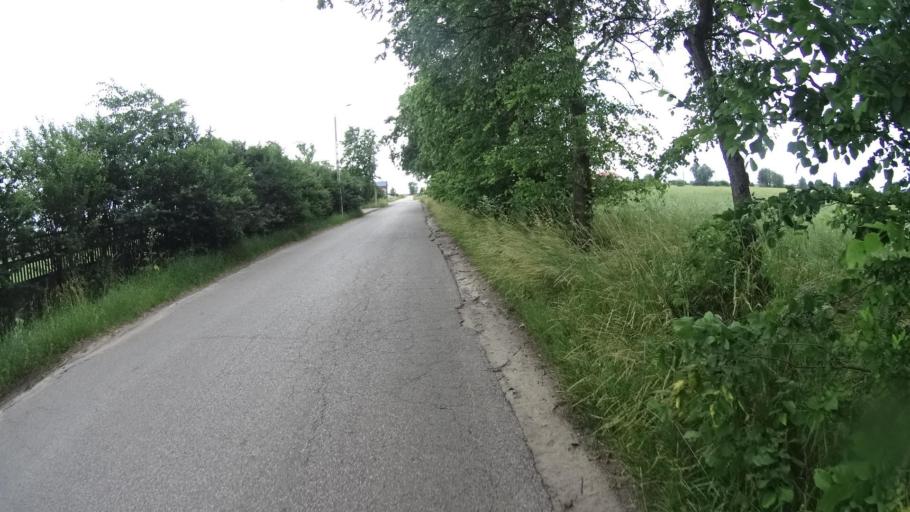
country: PL
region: Masovian Voivodeship
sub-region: Powiat piaseczynski
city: Tarczyn
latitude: 52.0329
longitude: 20.8225
